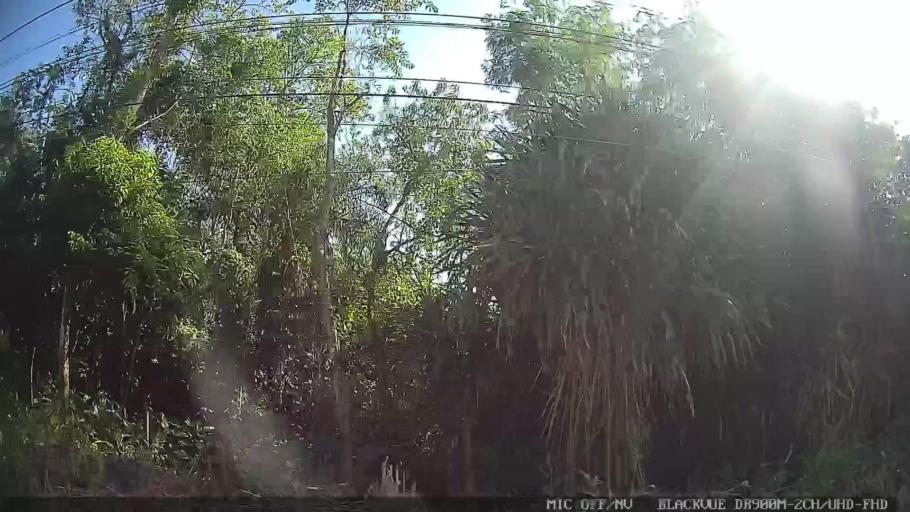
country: BR
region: Sao Paulo
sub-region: Guaruja
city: Guaruja
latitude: -24.0093
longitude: -46.2901
